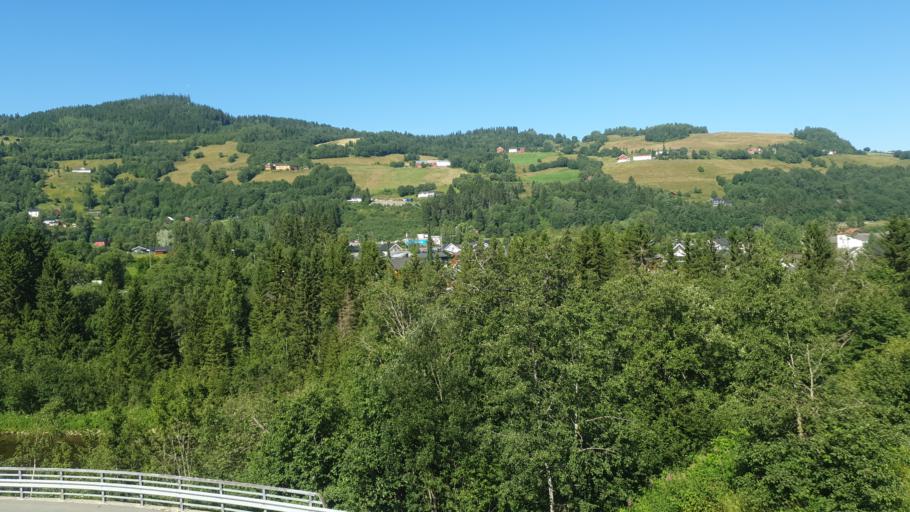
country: NO
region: Sor-Trondelag
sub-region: Meldal
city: Meldal
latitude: 63.1675
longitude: 9.7451
